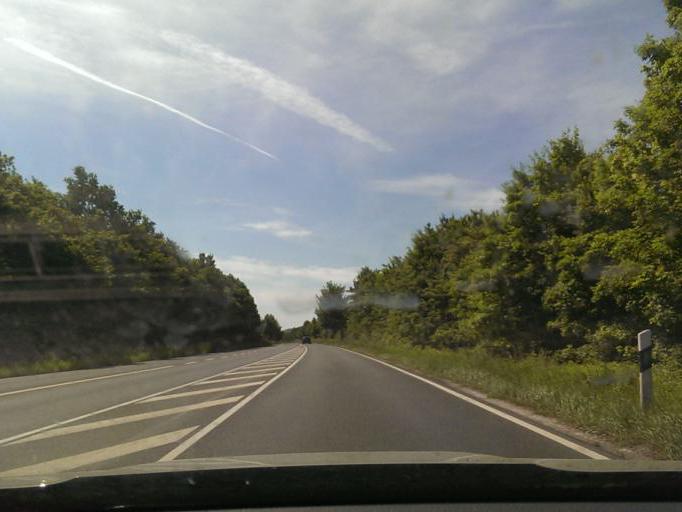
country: DE
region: Lower Saxony
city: Banteln
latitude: 52.0793
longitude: 9.7432
